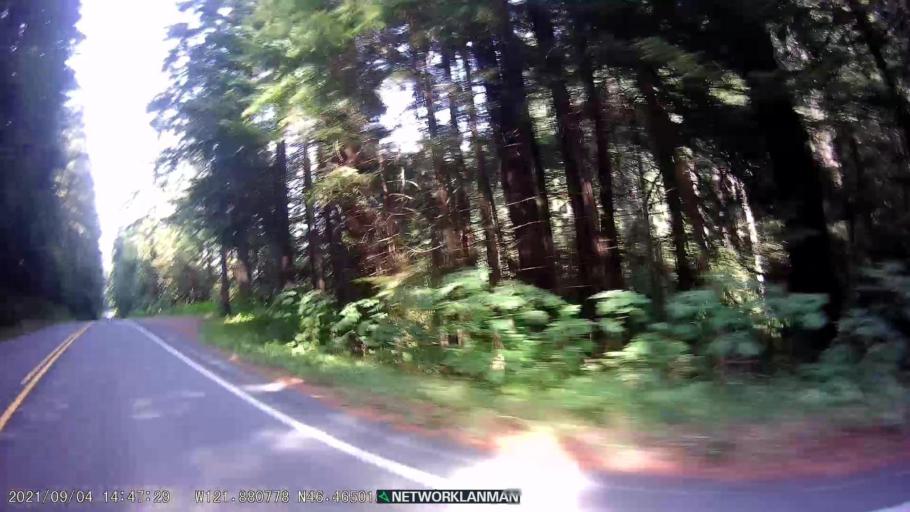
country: US
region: Washington
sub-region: Lewis County
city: Morton
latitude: 46.4652
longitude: -121.8810
